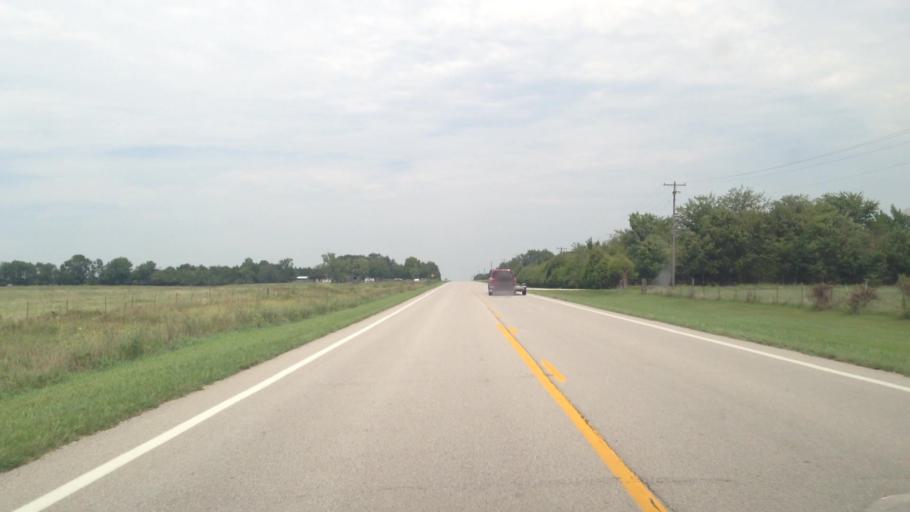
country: US
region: Kansas
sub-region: Neosho County
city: Erie
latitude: 37.6478
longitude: -95.2516
